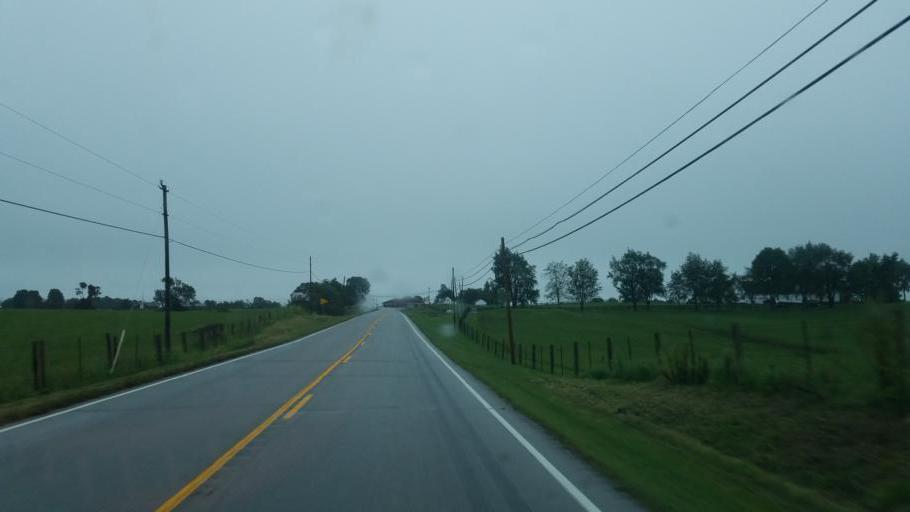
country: US
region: Kentucky
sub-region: Fleming County
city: Flemingsburg
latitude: 38.3958
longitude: -83.6953
